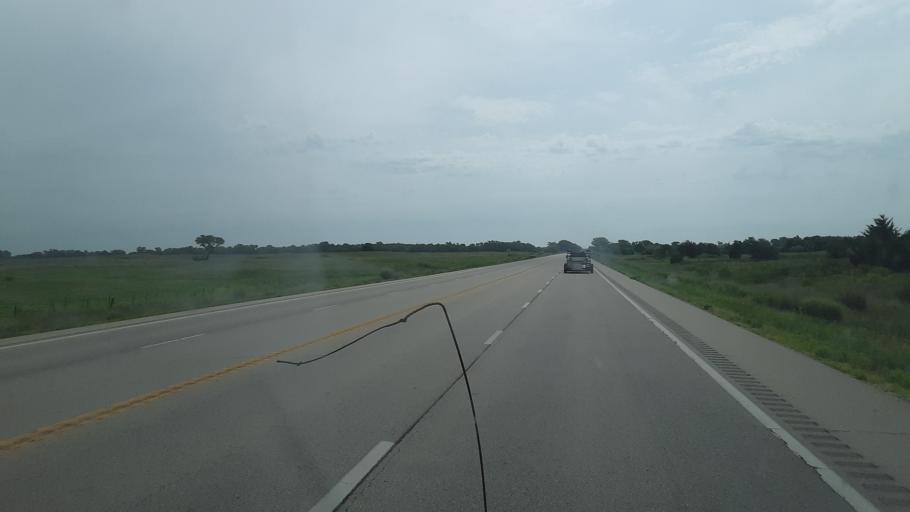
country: US
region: Kansas
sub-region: Rice County
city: Sterling
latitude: 37.9848
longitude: -98.3041
